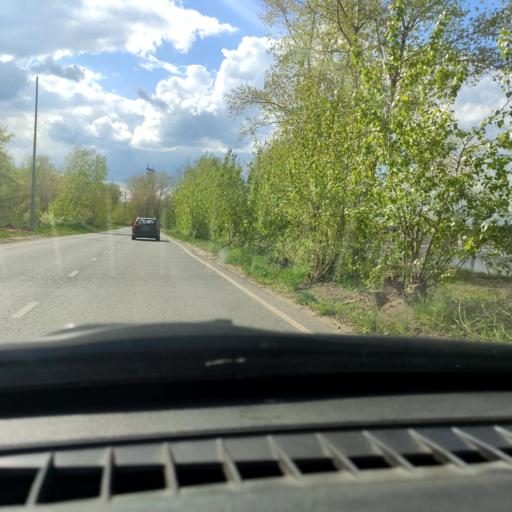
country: RU
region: Samara
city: Zhigulevsk
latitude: 53.4609
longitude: 49.5127
